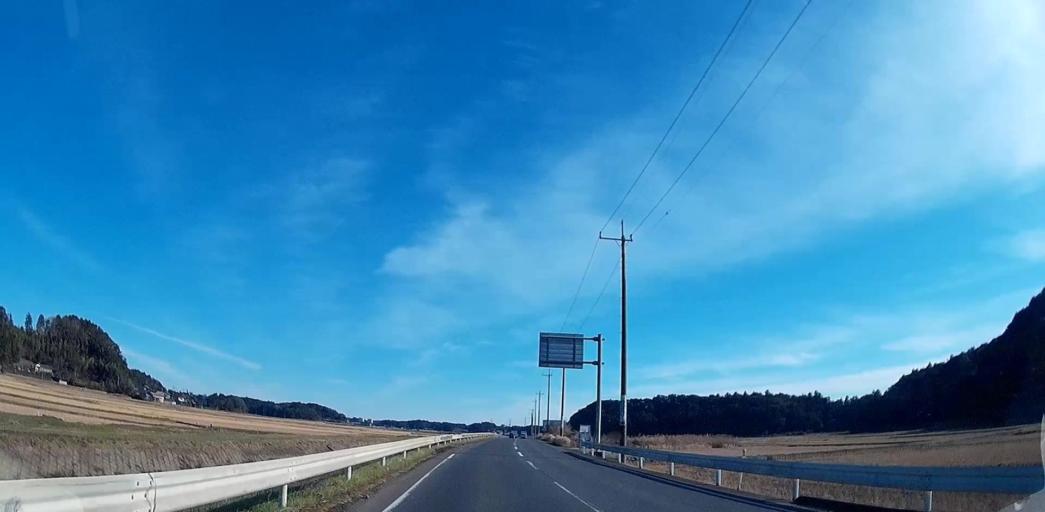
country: JP
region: Chiba
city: Yokaichiba
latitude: 35.7353
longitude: 140.5033
